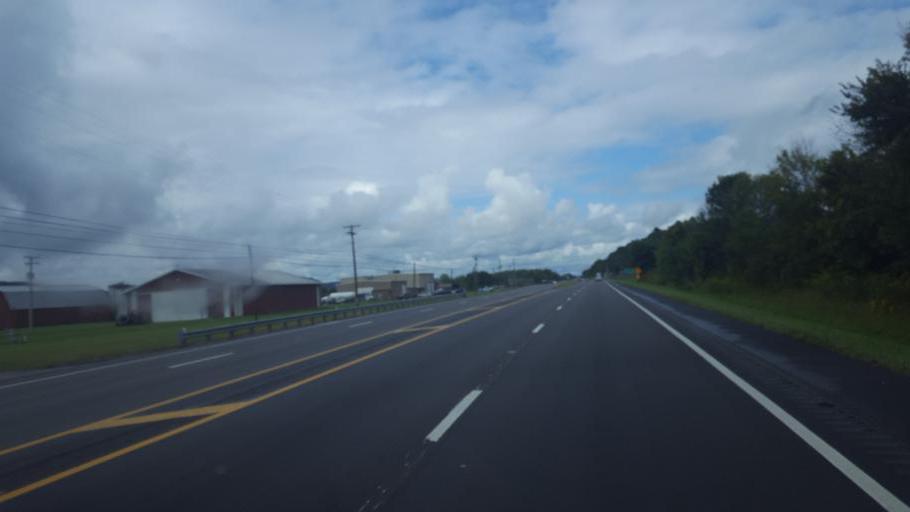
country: US
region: Ohio
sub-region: Scioto County
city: Lucasville
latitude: 38.8574
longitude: -82.9880
